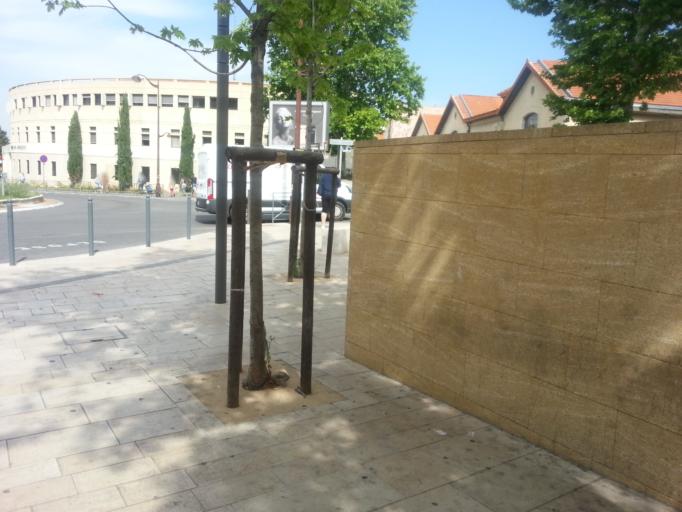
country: FR
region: Provence-Alpes-Cote d'Azur
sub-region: Departement des Bouches-du-Rhone
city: Aix-en-Provence
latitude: 43.5237
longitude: 5.4396
